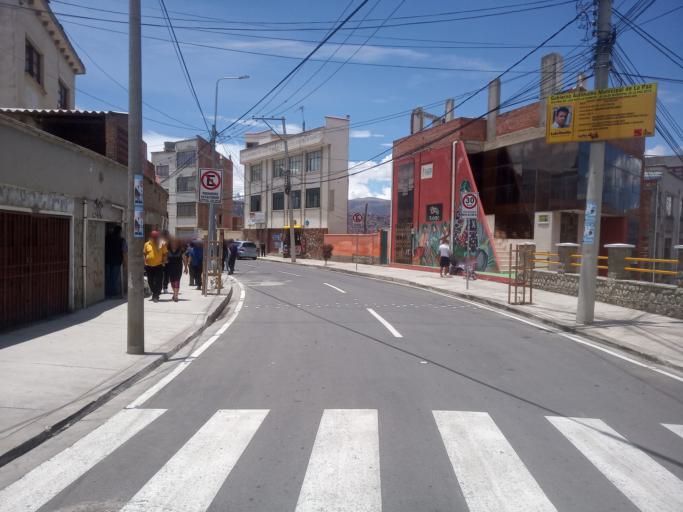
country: BO
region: La Paz
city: La Paz
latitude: -16.5134
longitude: -68.1339
